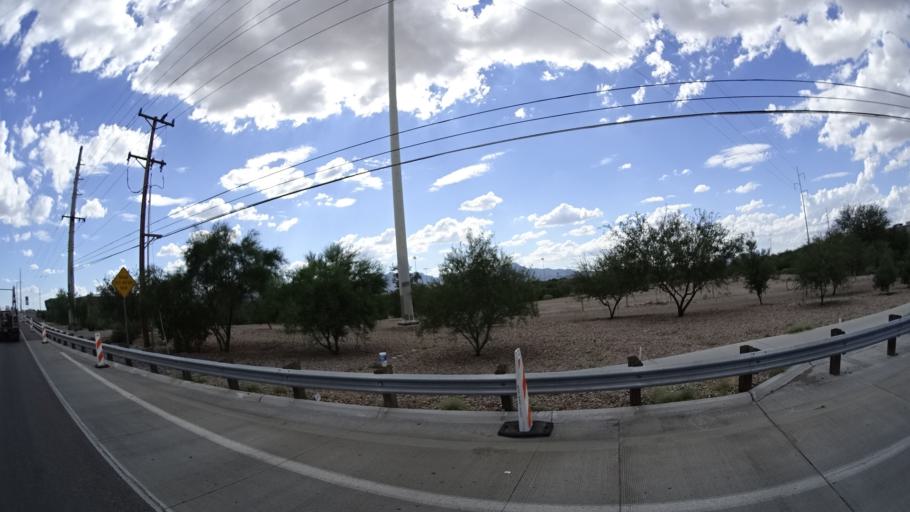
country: US
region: Arizona
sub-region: Pima County
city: Flowing Wells
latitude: 32.3039
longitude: -111.0121
